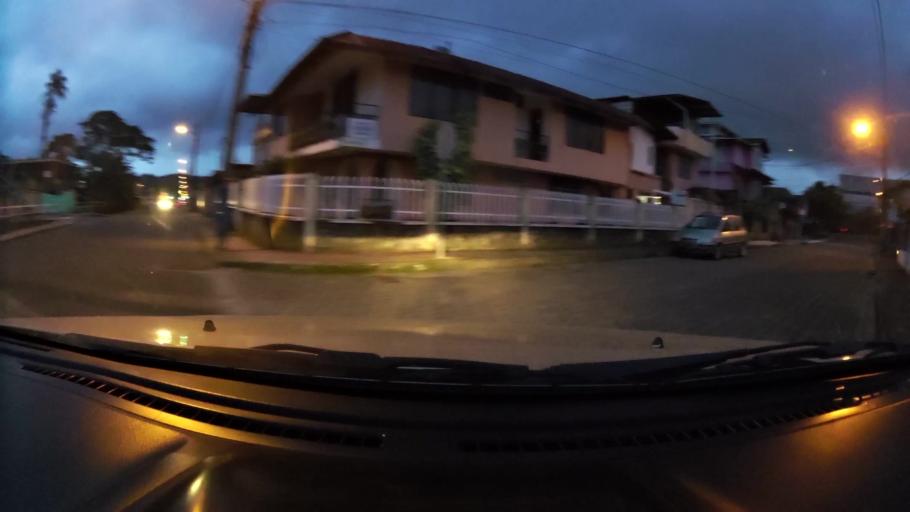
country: EC
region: Pastaza
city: Puyo
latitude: -1.4800
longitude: -78.0045
